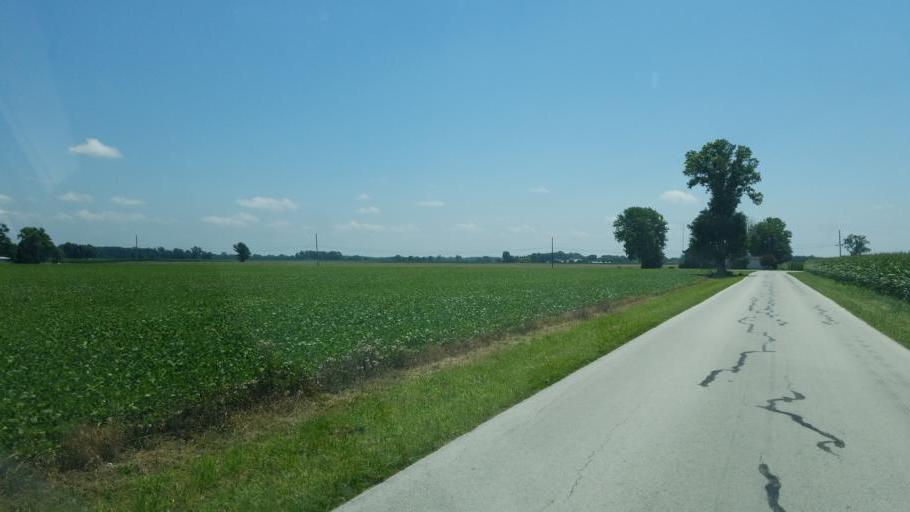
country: US
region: Ohio
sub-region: Sandusky County
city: Fremont
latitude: 41.3832
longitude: -83.0779
